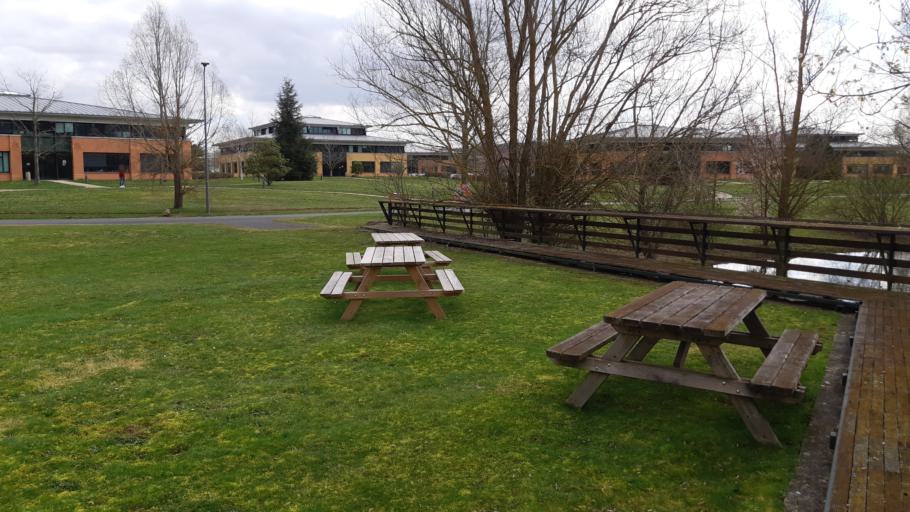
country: FR
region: Ile-de-France
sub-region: Departement de l'Essonne
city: Bondoufle
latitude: 48.5988
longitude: 2.3641
